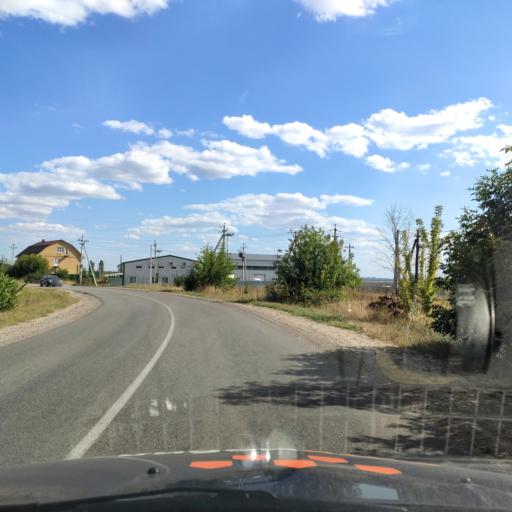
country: RU
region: Voronezj
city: Somovo
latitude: 51.6995
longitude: 39.3742
